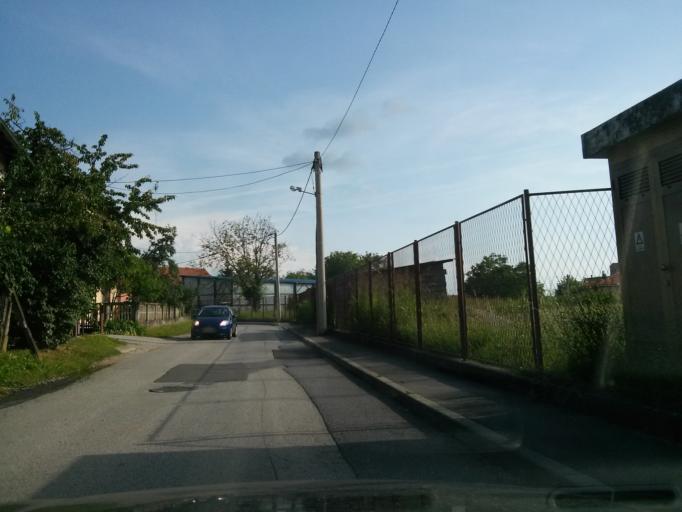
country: HR
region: Grad Zagreb
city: Zadvorsko
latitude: 45.7676
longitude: 15.9352
